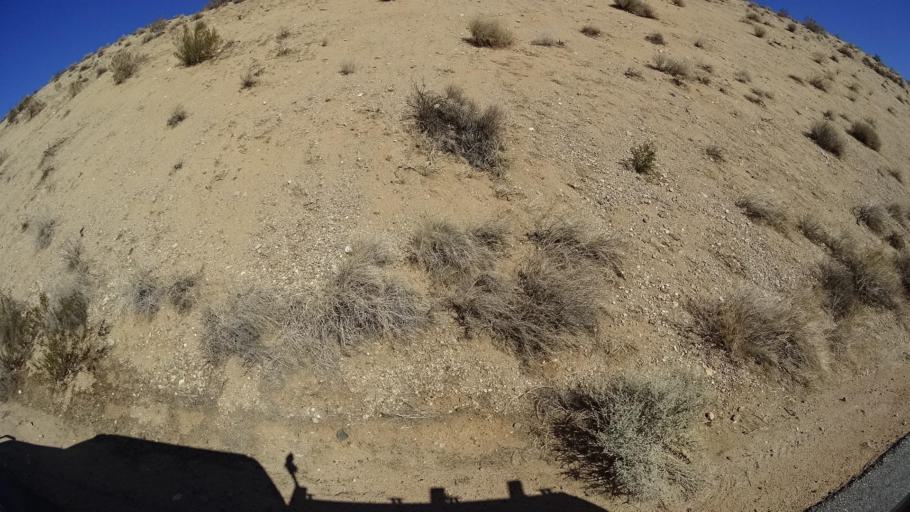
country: US
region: California
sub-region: Kern County
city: California City
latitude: 35.3022
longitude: -118.0056
